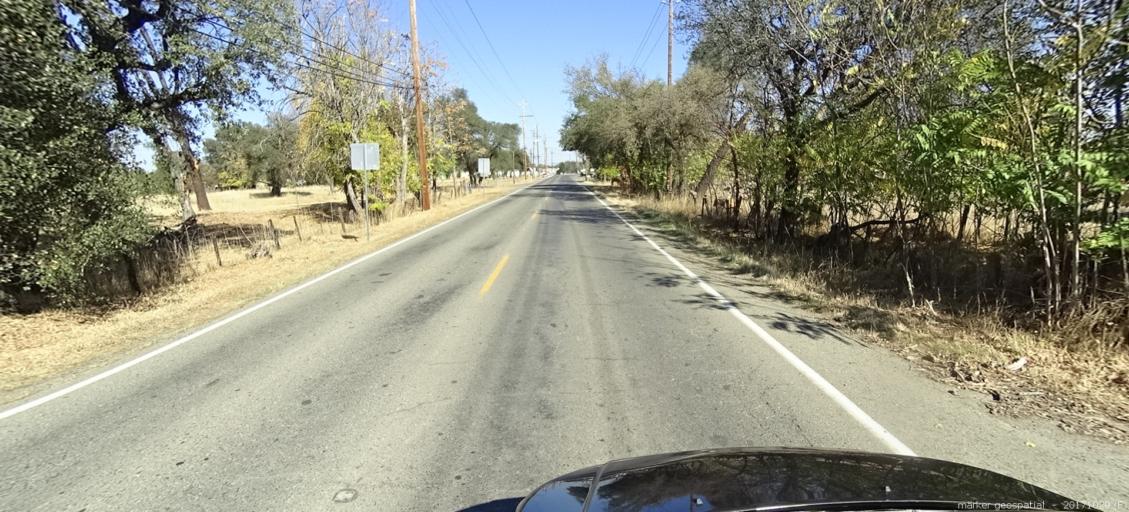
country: US
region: California
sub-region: Shasta County
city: Redding
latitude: 40.5143
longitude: -122.3844
